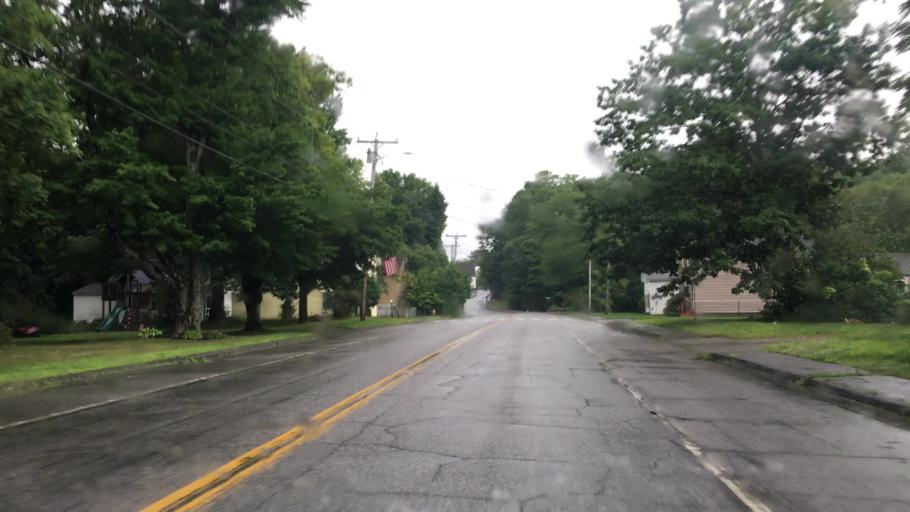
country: US
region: Maine
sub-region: Kennebec County
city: Pittston
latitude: 44.1819
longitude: -69.7568
